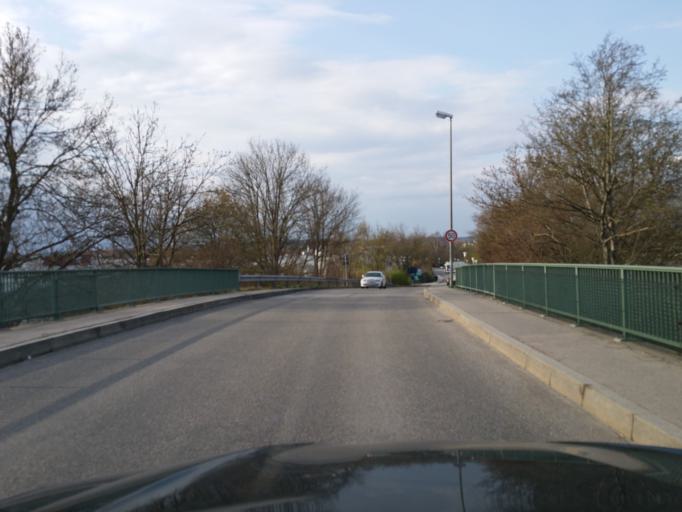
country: DE
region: Bavaria
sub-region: Lower Bavaria
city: Ergolding
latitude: 48.5598
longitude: 12.1681
